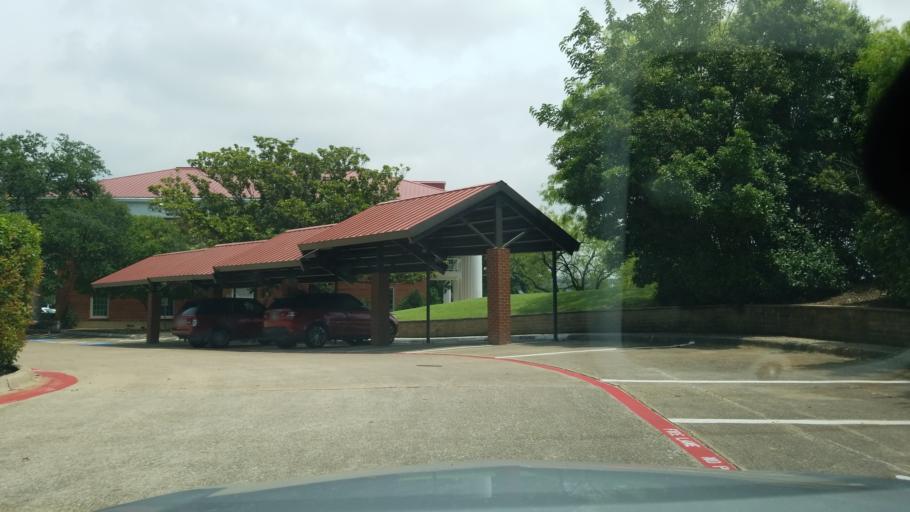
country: US
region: Texas
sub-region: Dallas County
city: Irving
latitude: 32.8570
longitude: -96.9359
